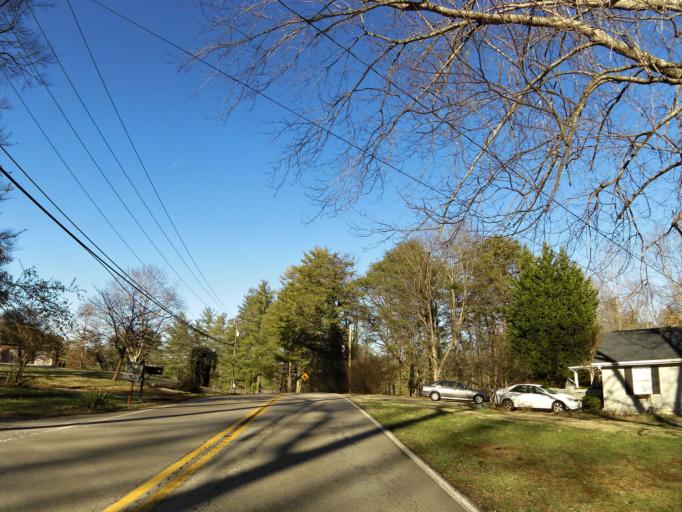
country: US
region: Tennessee
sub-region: Knox County
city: Knoxville
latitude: 35.8908
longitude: -83.9747
